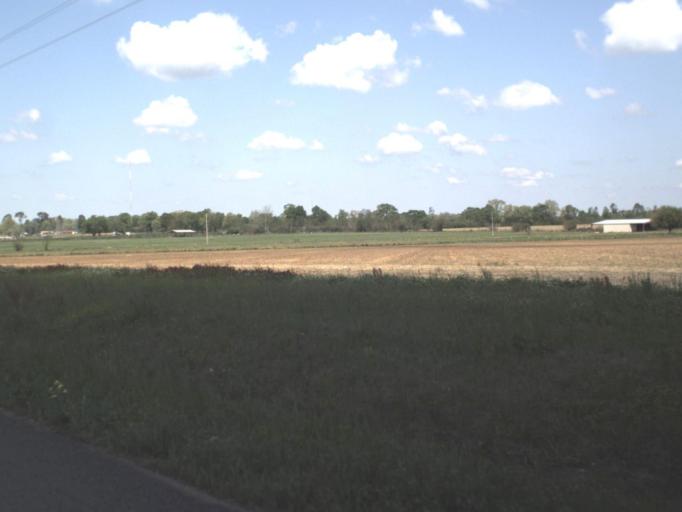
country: US
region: Alabama
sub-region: Escambia County
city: East Brewton
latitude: 30.8996
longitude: -87.0156
